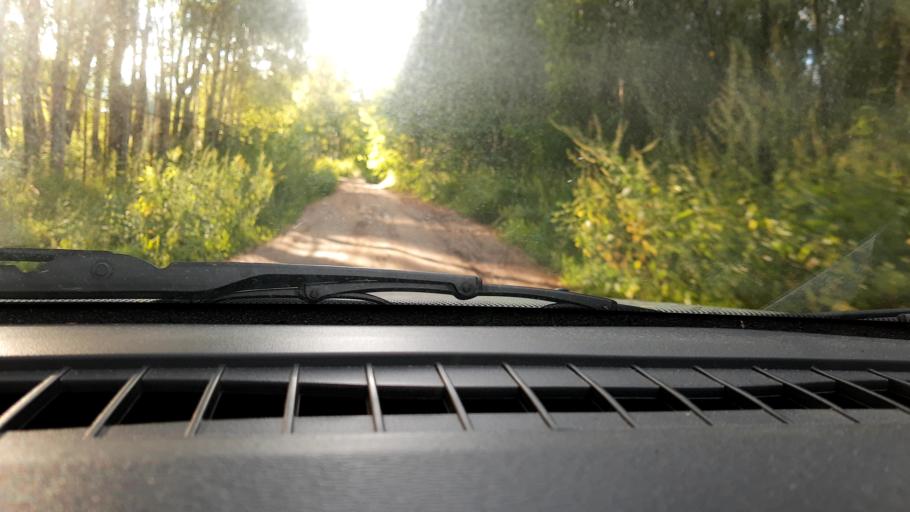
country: RU
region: Nizjnij Novgorod
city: Sitniki
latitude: 56.4515
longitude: 44.0193
